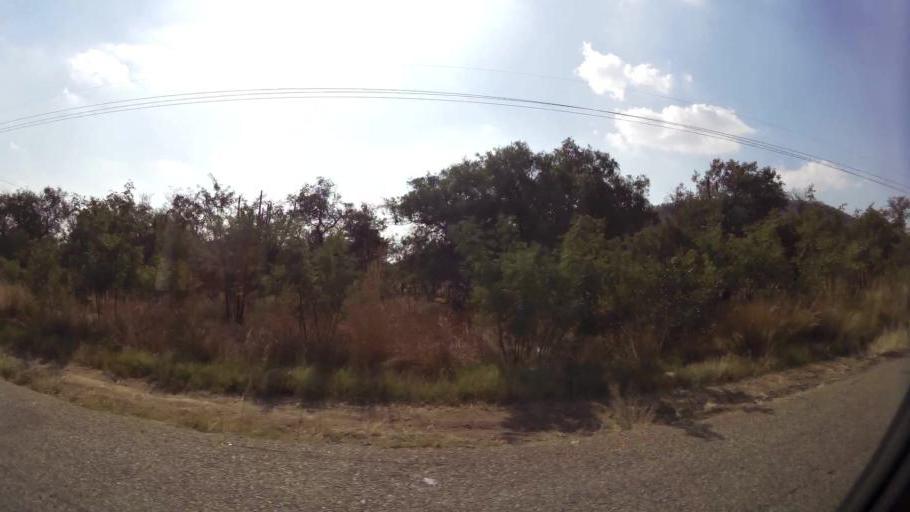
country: ZA
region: North-West
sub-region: Bojanala Platinum District Municipality
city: Rustenburg
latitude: -25.6326
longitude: 27.1747
